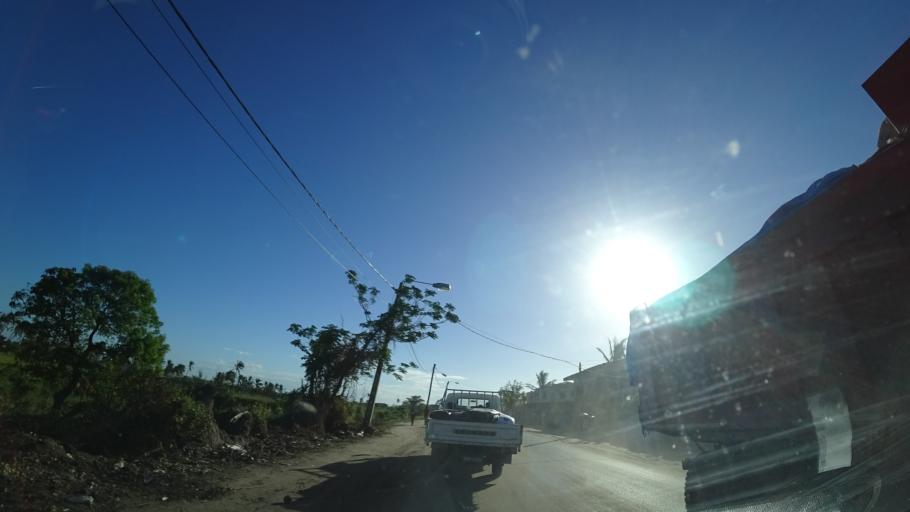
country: MZ
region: Sofala
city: Beira
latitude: -19.7803
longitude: 34.8743
